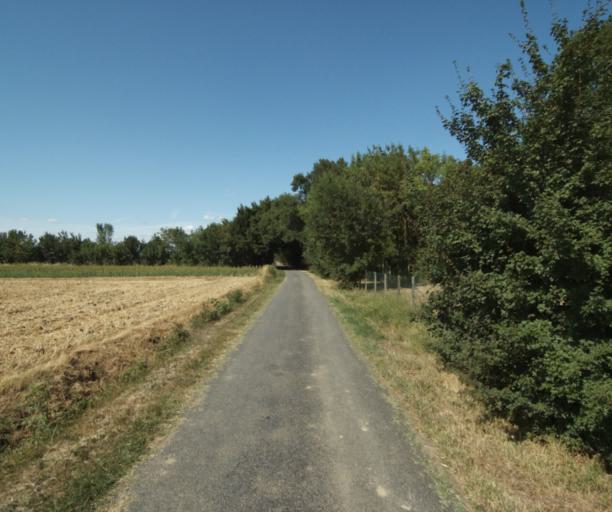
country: FR
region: Midi-Pyrenees
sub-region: Departement de la Haute-Garonne
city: Revel
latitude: 43.4973
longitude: 1.9659
